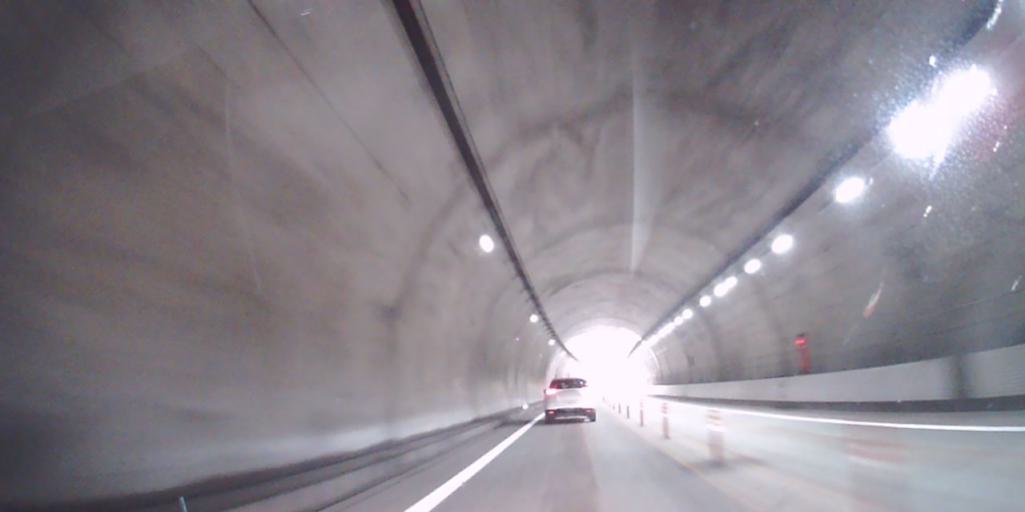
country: JP
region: Hokkaido
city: Date
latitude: 42.5756
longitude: 140.7368
